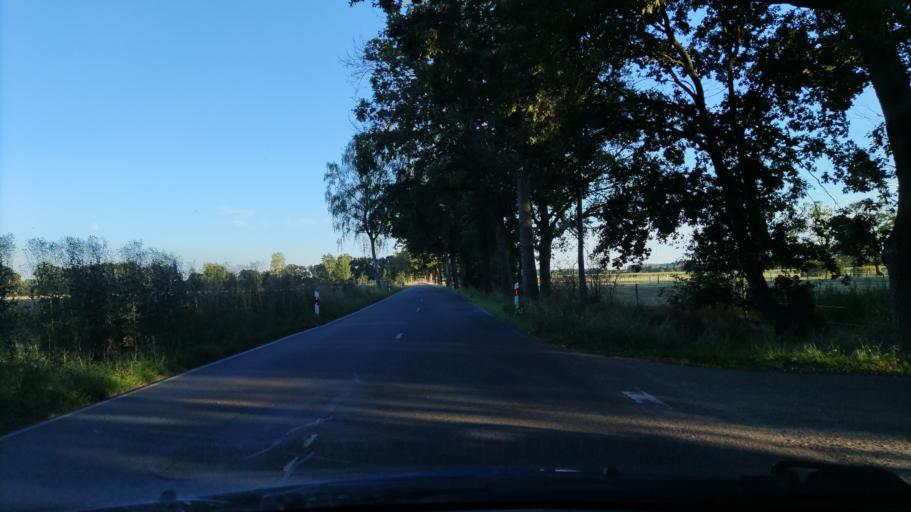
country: DE
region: Lower Saxony
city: Luechow
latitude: 52.9992
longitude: 11.1523
